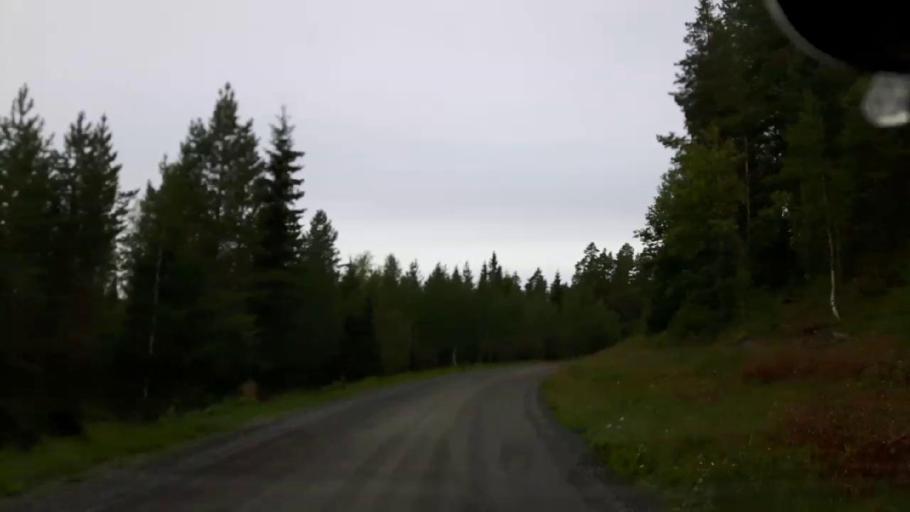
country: SE
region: Jaemtland
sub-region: Krokoms Kommun
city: Krokom
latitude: 63.3033
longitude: 14.3472
